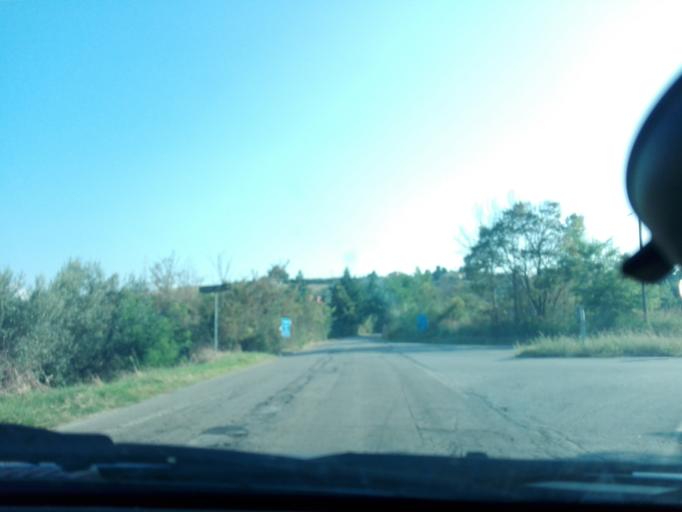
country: IT
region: Abruzzo
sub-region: Provincia di Pescara
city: Cappelle sul Tavo
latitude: 42.4525
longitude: 14.0904
